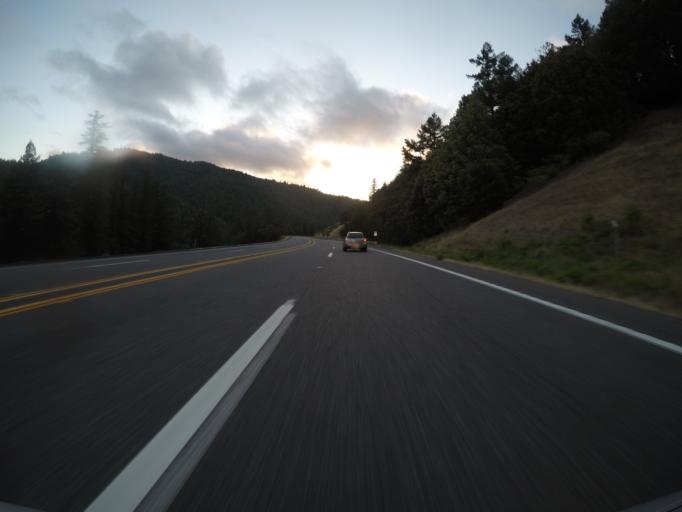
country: US
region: California
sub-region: Humboldt County
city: Redway
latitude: 40.0472
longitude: -123.7853
